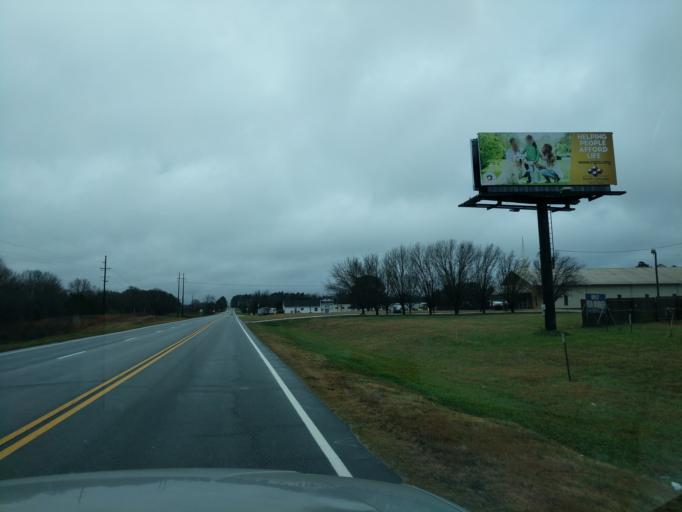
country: US
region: Georgia
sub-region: Franklin County
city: Lavonia
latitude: 34.4091
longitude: -83.1001
